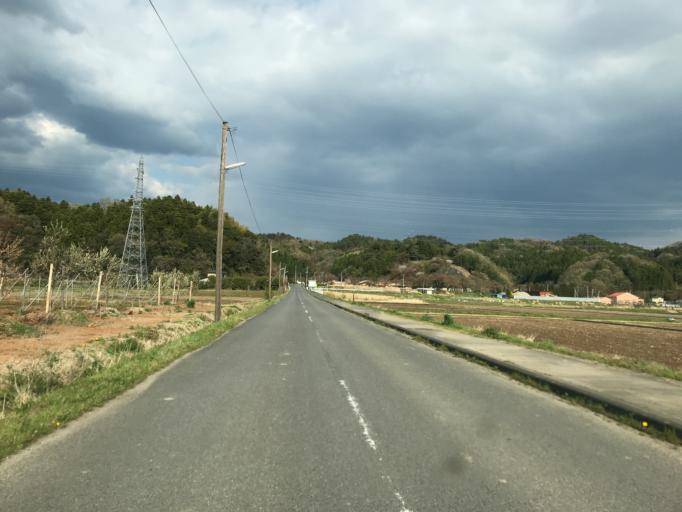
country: JP
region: Fukushima
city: Iwaki
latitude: 37.0882
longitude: 140.8803
